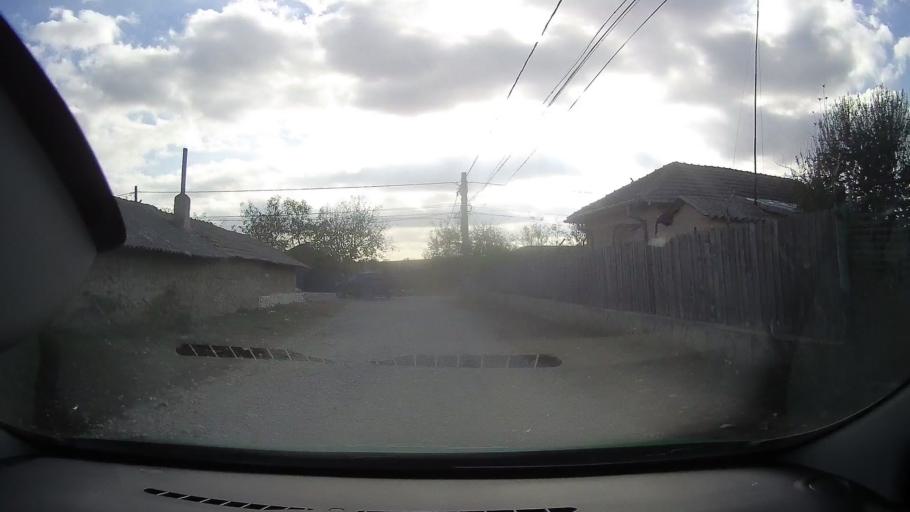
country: RO
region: Constanta
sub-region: Comuna Sacele
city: Sacele
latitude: 44.4890
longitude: 28.6370
